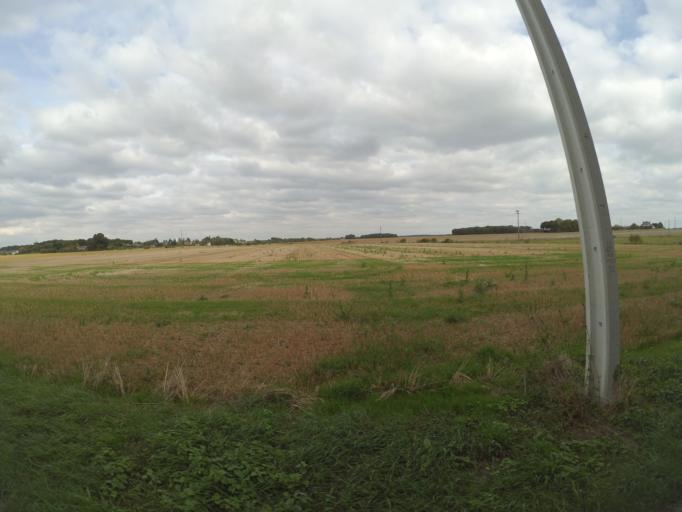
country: FR
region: Centre
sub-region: Departement d'Indre-et-Loire
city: Nazelles-Negron
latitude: 47.4805
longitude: 0.9414
